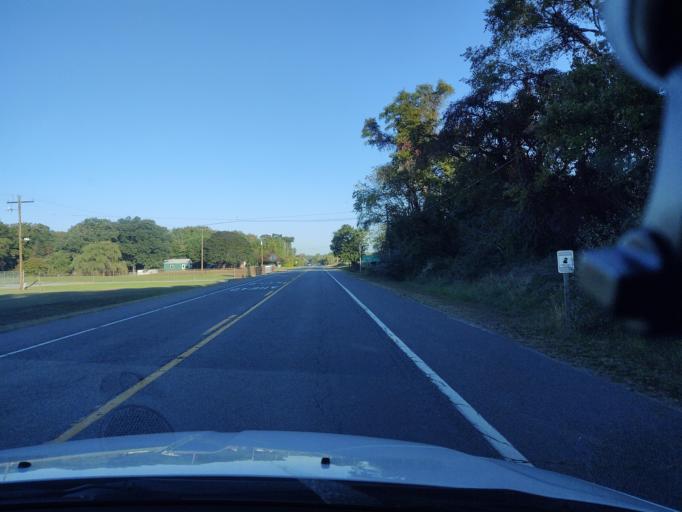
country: US
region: Maryland
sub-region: Queen Anne's County
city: Kingstown
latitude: 39.2332
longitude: -75.9145
